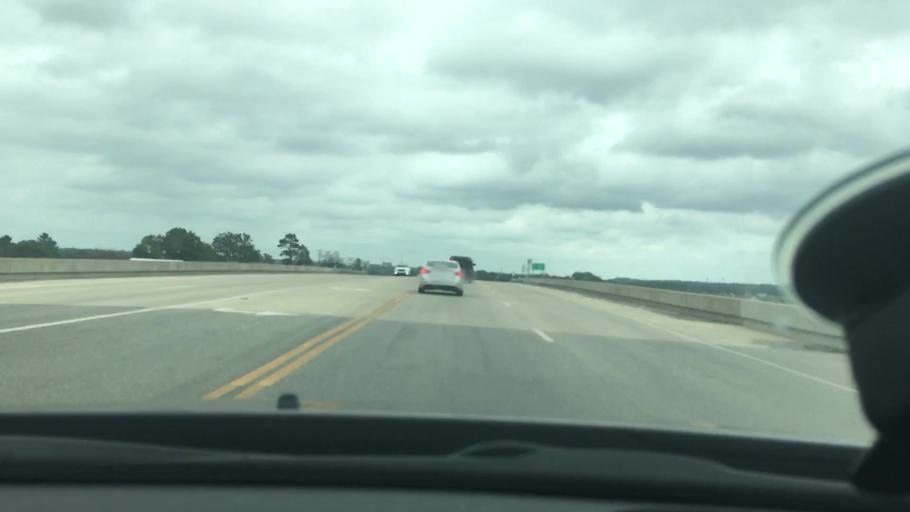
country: US
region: Oklahoma
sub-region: Bryan County
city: Durant
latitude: 33.9650
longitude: -96.3731
